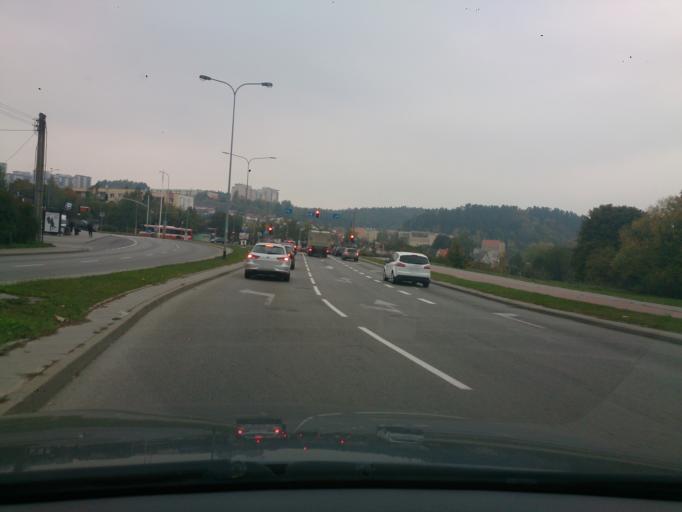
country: PL
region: Pomeranian Voivodeship
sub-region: Powiat gdanski
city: Kowale
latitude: 54.3731
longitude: 18.5688
